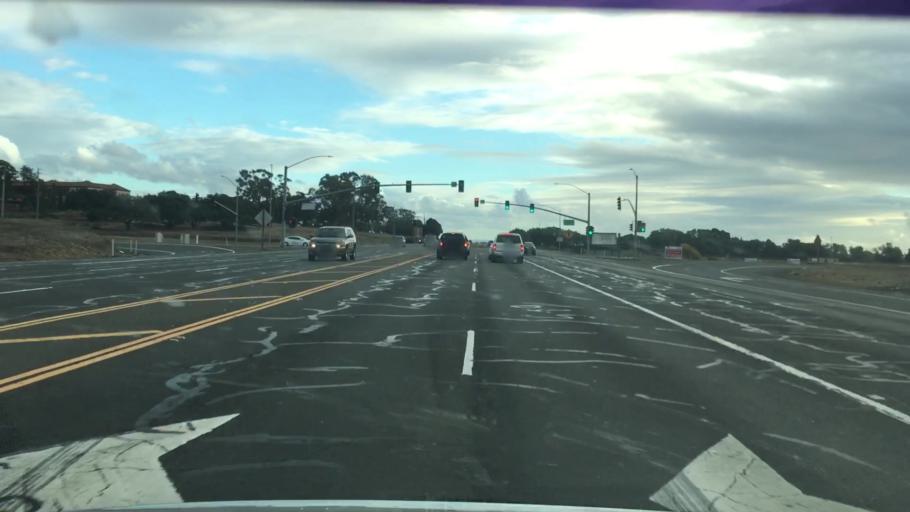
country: US
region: California
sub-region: Napa County
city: American Canyon
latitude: 38.2241
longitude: -122.2581
